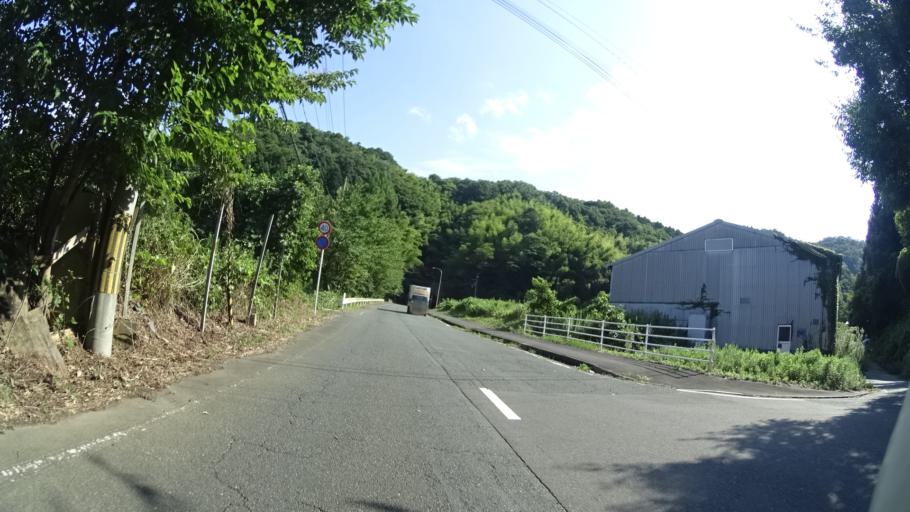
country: JP
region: Kyoto
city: Maizuru
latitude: 35.4767
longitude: 135.3162
